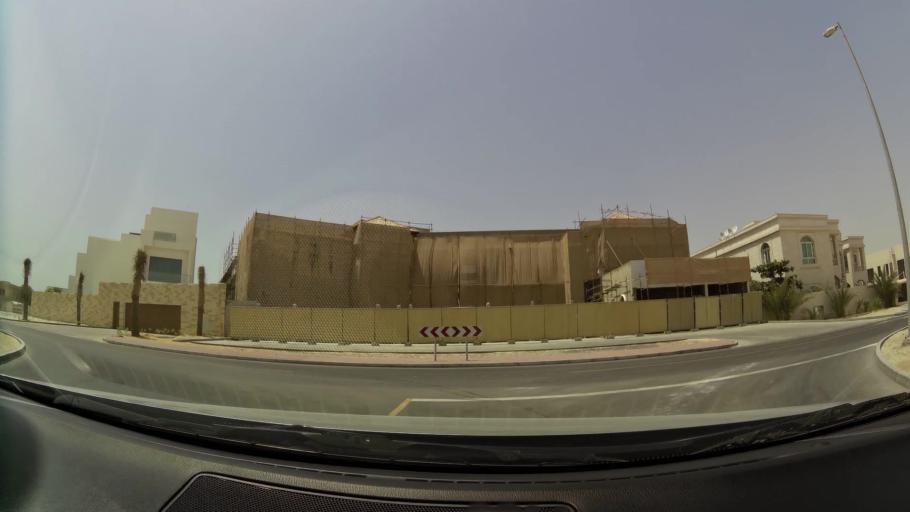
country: AE
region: Dubai
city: Dubai
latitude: 25.1324
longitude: 55.1960
